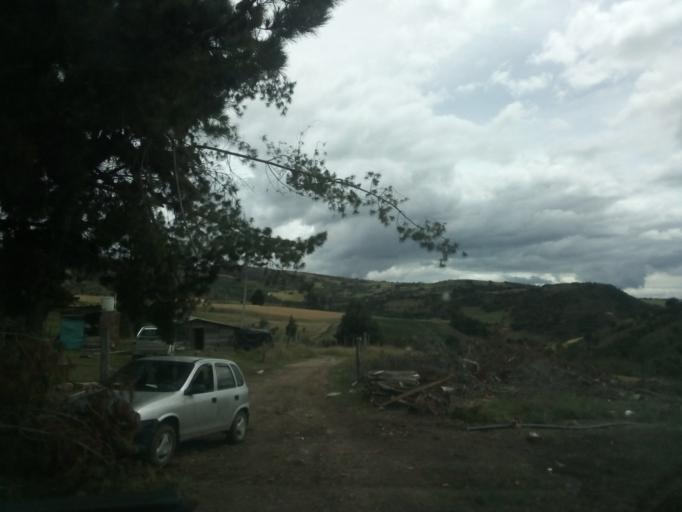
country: CO
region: Boyaca
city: Toca
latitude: 5.5991
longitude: -73.1159
